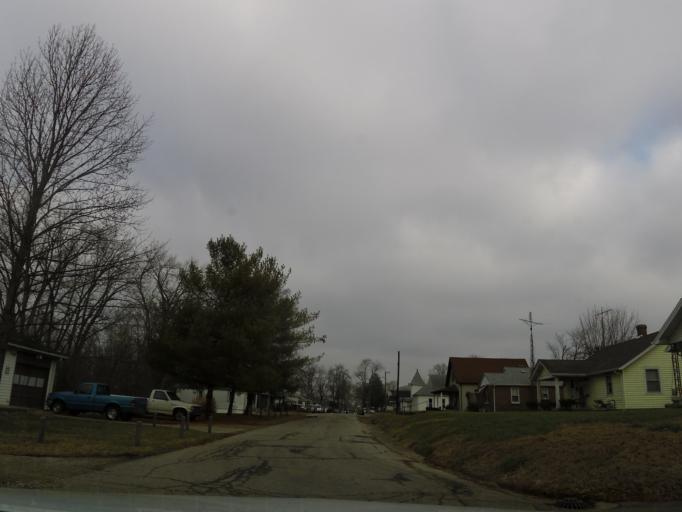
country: US
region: Indiana
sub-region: Bartholomew County
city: Columbus
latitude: 39.1955
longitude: -85.9071
